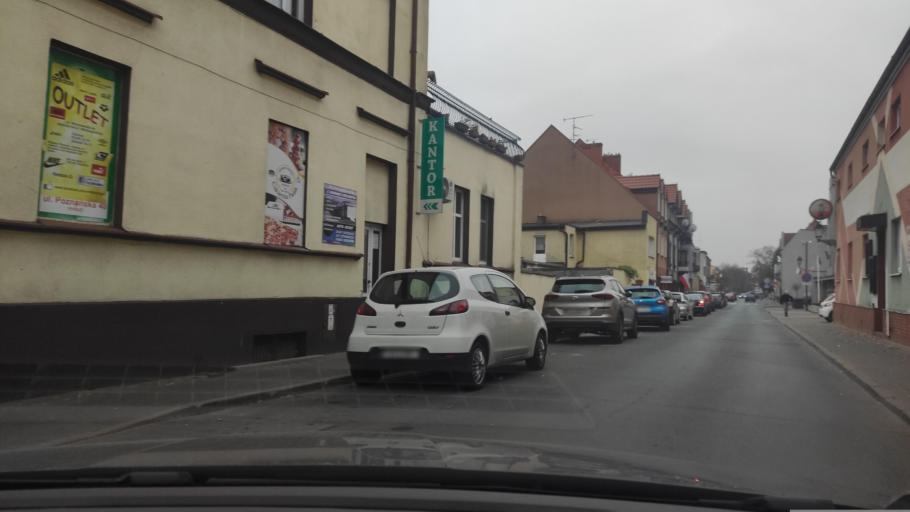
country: PL
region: Greater Poland Voivodeship
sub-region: Powiat poznanski
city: Kostrzyn
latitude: 52.3980
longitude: 17.2260
